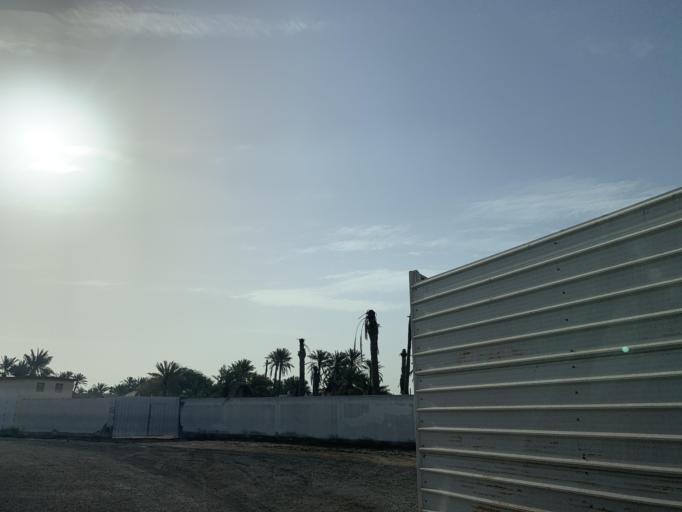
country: BH
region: Manama
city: Manama
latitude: 26.1801
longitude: 50.5847
